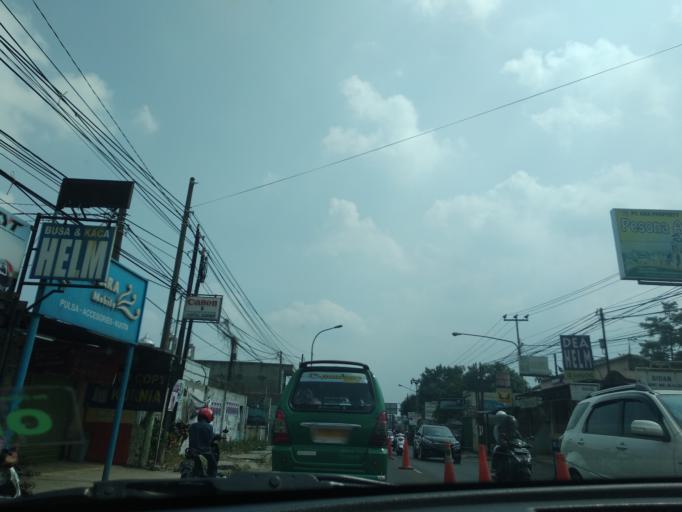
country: ID
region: West Java
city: Cimahi
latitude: -6.8685
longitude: 107.5228
